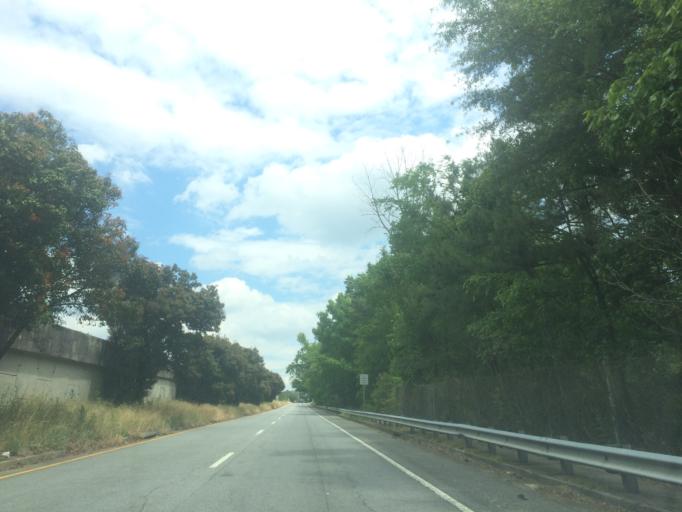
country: US
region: Georgia
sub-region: DeKalb County
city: North Druid Hills
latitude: 33.8515
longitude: -84.3005
